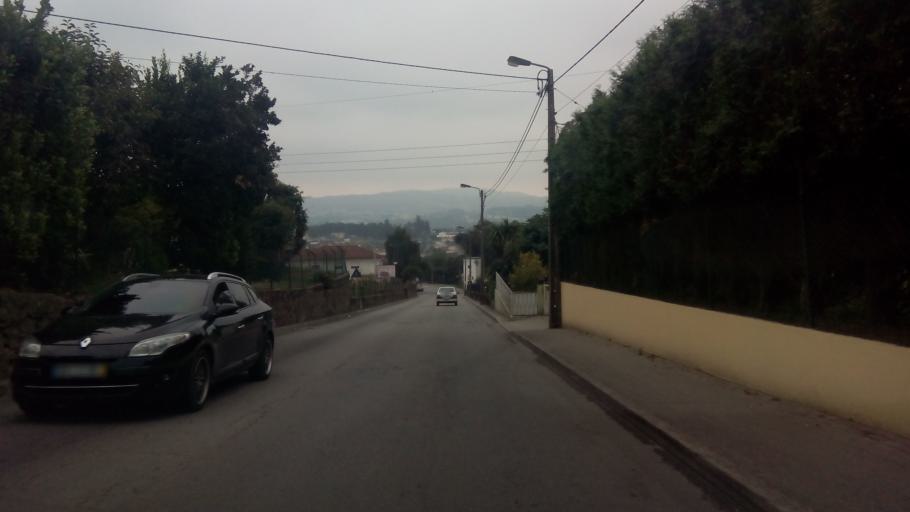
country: PT
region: Porto
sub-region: Paredes
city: Madalena
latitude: 41.2164
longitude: -8.3533
